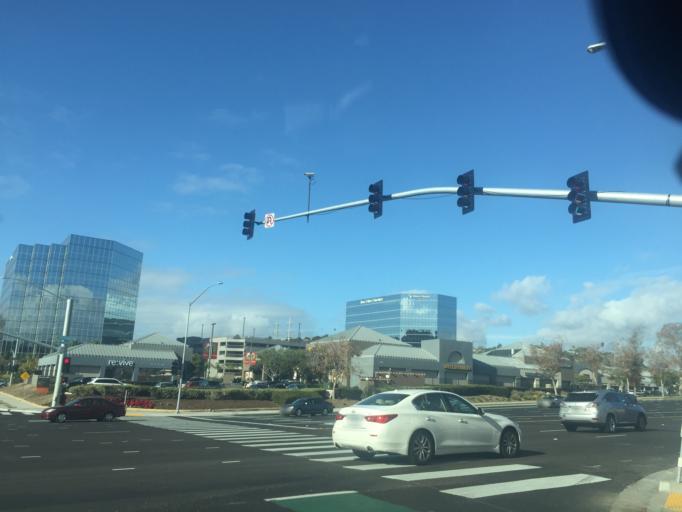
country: US
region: California
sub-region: San Diego County
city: San Diego
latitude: 32.7726
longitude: -117.1571
